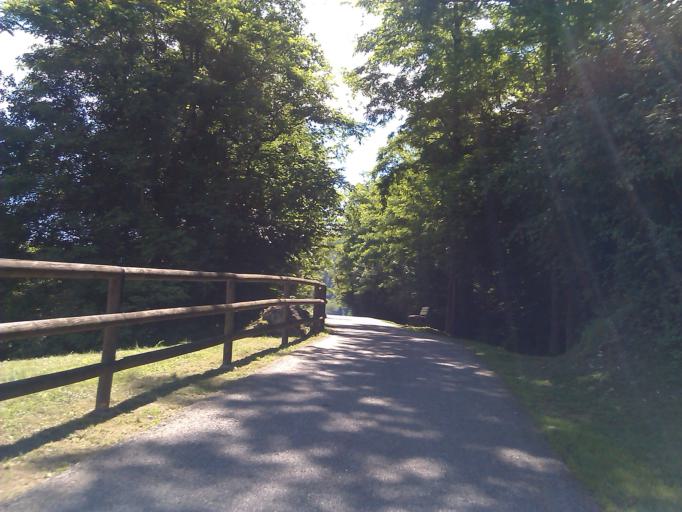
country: IT
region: Trentino-Alto Adige
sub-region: Provincia di Trento
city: Castelnuovo
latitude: 46.0499
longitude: 11.4789
